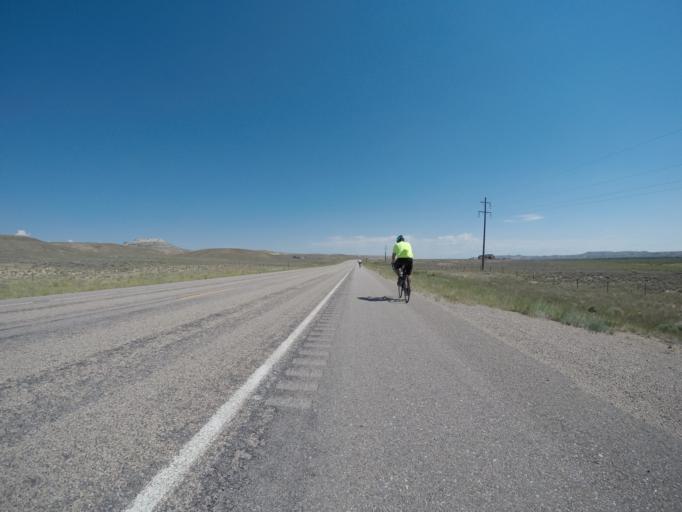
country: US
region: Wyoming
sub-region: Sublette County
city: Marbleton
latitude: 42.3666
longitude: -110.1513
